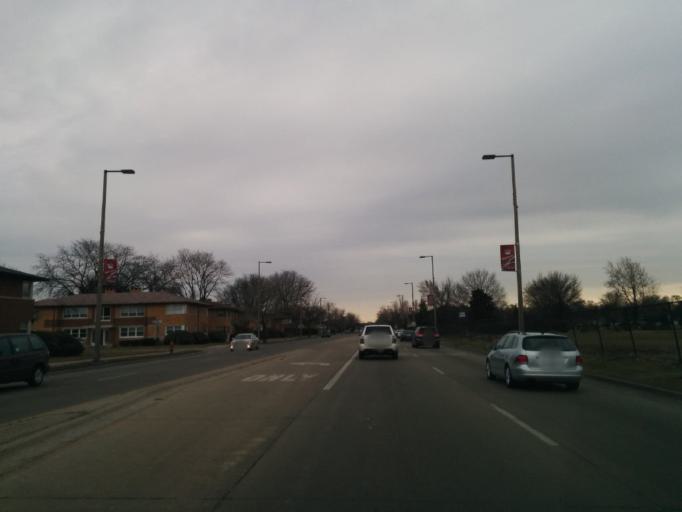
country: US
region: Illinois
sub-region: Cook County
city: Westchester
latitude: 41.8593
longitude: -87.8823
